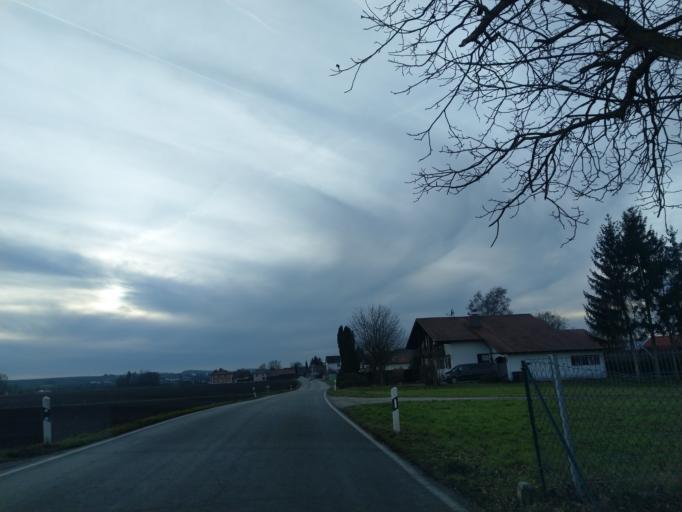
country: DE
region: Bavaria
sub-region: Lower Bavaria
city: Oberporing
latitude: 48.7139
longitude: 12.8476
